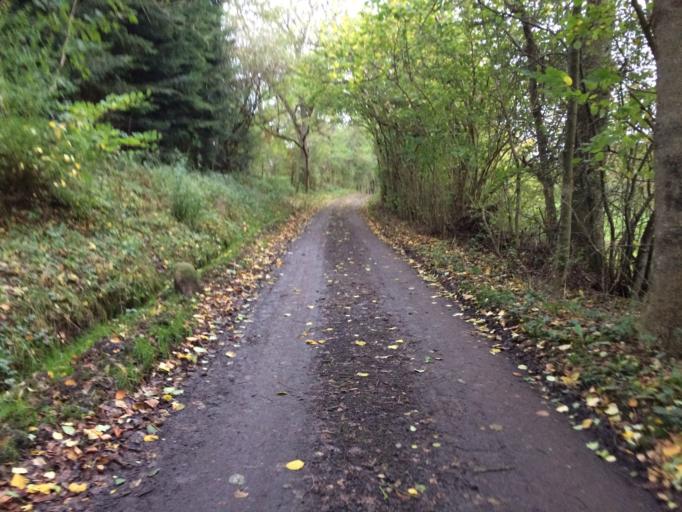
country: DK
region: South Denmark
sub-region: Vejle Kommune
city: Borkop
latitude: 55.6085
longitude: 9.6501
